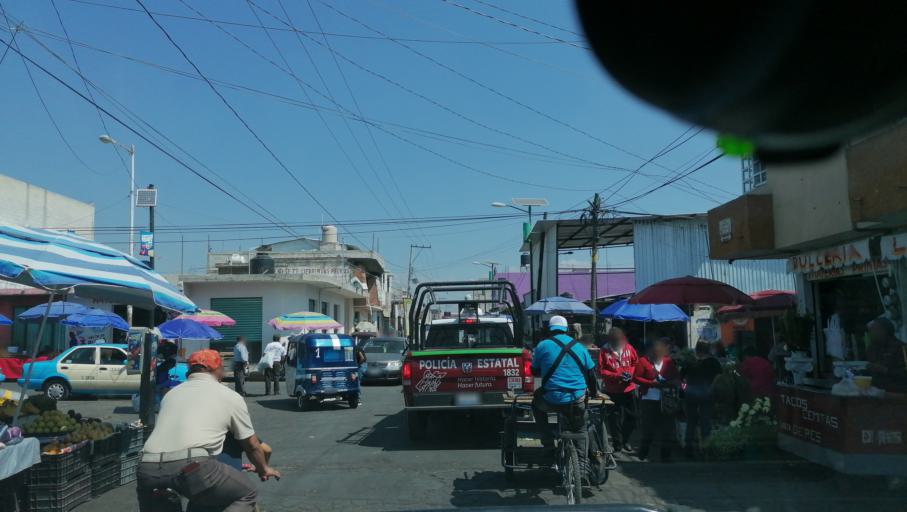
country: MX
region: Puebla
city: Huejotzingo
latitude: 19.1577
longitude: -98.4125
